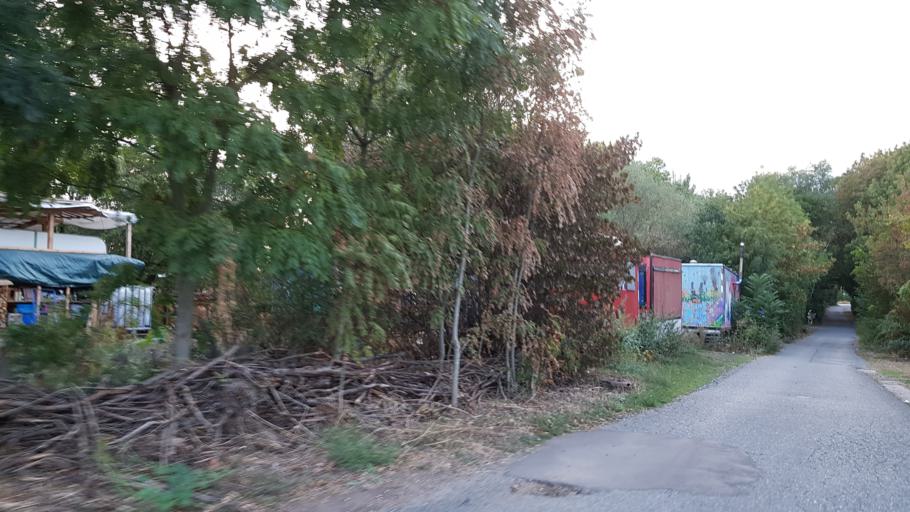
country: DE
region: Hesse
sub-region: Regierungsbezirk Darmstadt
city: Florsheim
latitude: 50.0021
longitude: 8.4251
